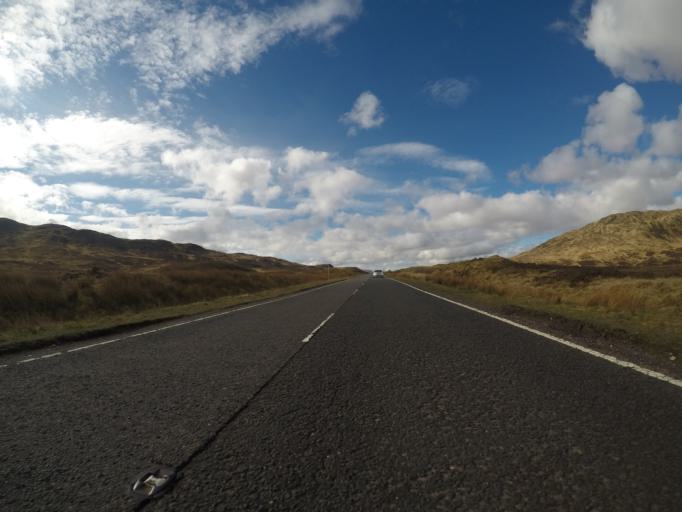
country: GB
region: Scotland
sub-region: Highland
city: Spean Bridge
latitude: 56.5911
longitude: -4.7452
